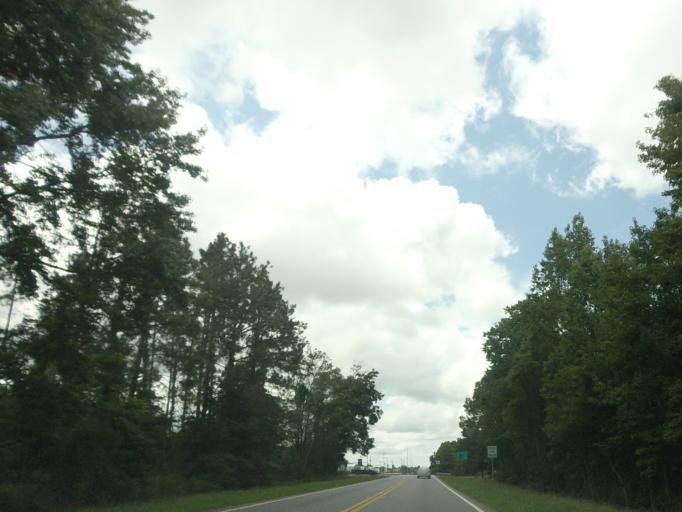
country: US
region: Georgia
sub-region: Bleckley County
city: Cochran
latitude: 32.3986
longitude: -83.3407
